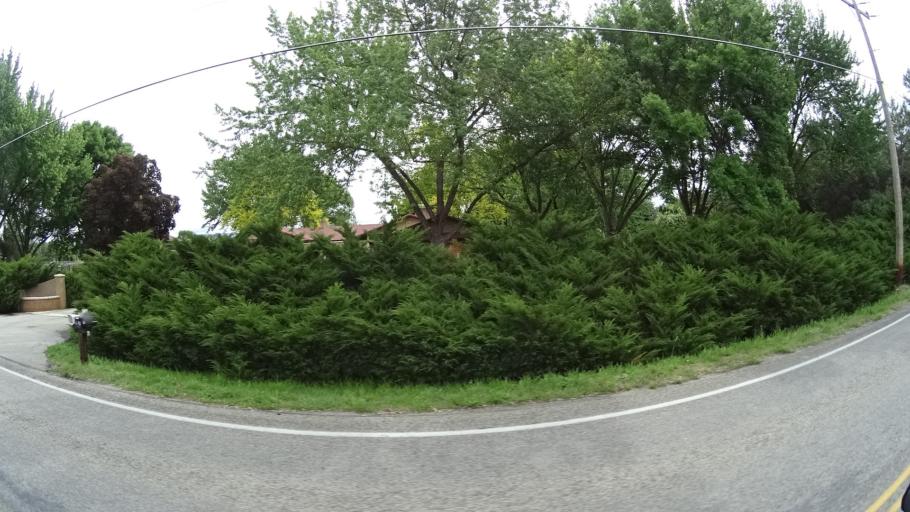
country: US
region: Idaho
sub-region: Ada County
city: Eagle
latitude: 43.7123
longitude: -116.3540
